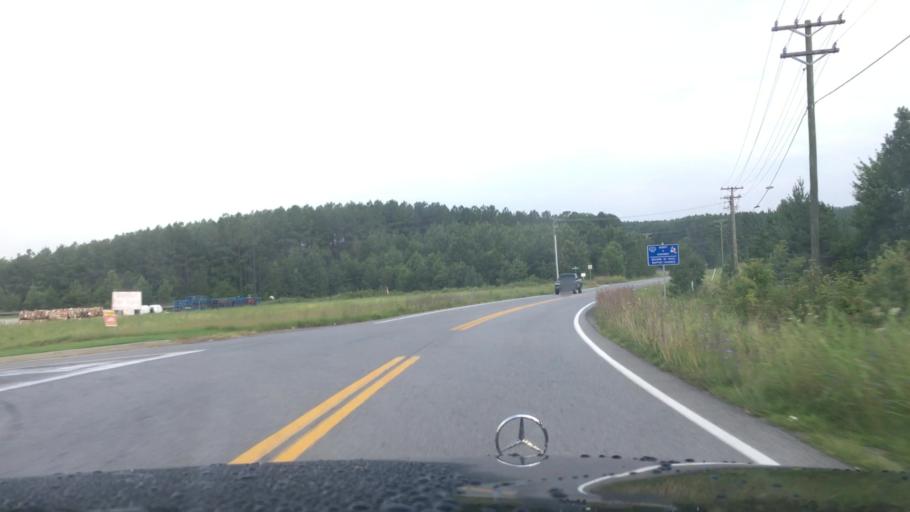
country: US
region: Virginia
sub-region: Campbell County
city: Altavista
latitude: 37.1443
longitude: -79.2685
